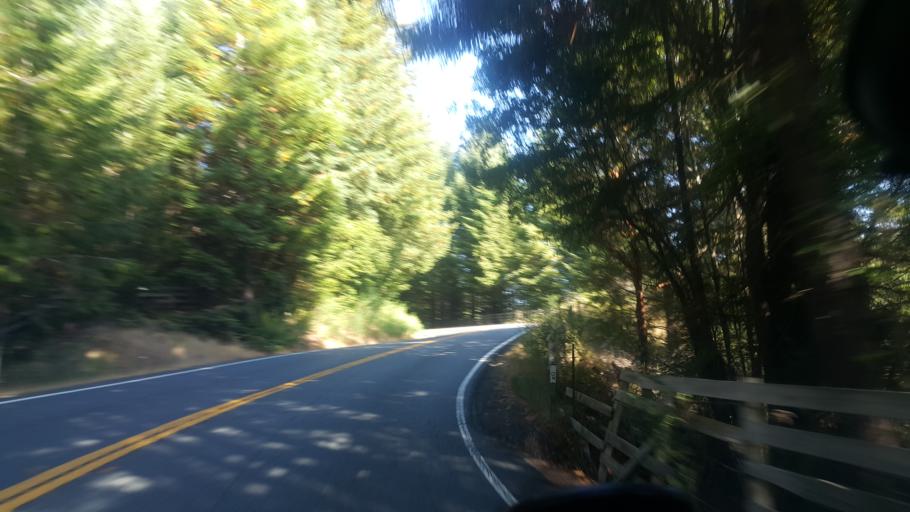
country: US
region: California
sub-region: Mendocino County
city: Fort Bragg
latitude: 39.3564
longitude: -123.6164
